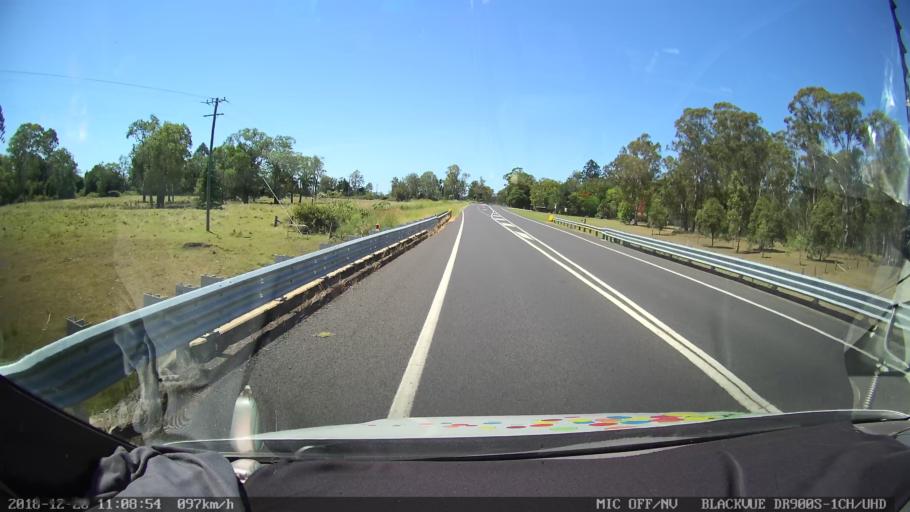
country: AU
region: New South Wales
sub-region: Richmond Valley
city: Casino
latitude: -28.9286
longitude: 153.0045
